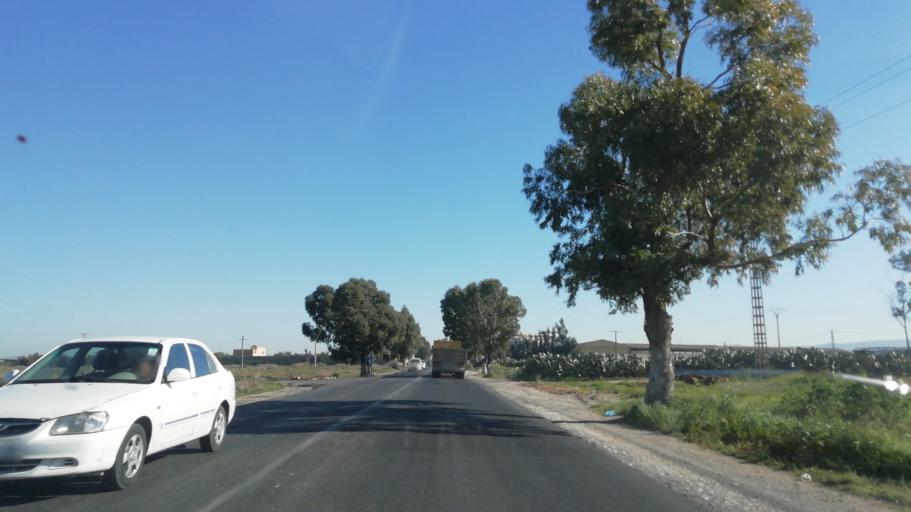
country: DZ
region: Relizane
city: Zemoura
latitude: 35.7562
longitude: 0.6743
